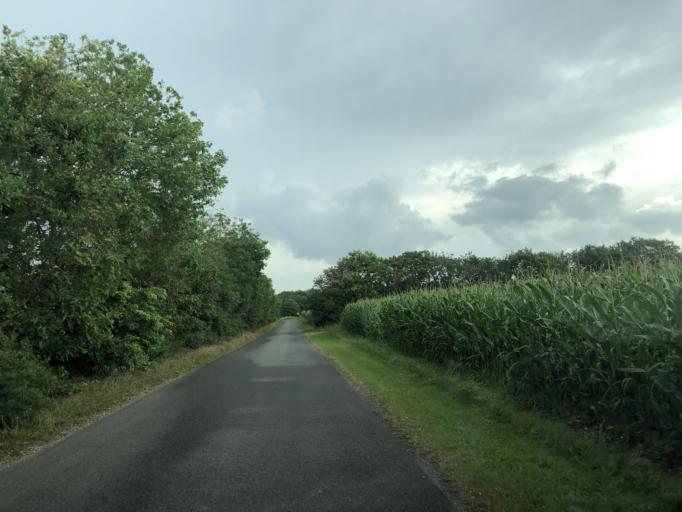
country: DK
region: Central Jutland
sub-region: Ringkobing-Skjern Kommune
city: Skjern
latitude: 55.8885
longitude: 8.4420
